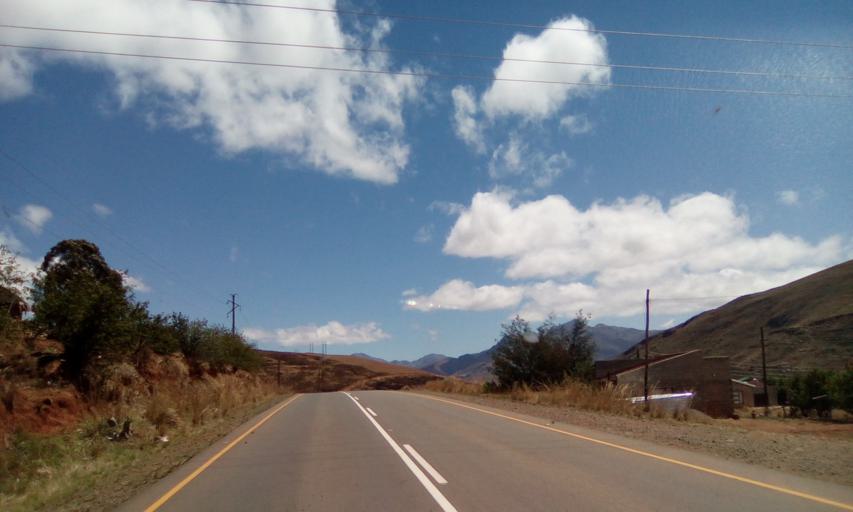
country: LS
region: Qacha's Nek
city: Qacha's Nek
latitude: -30.0913
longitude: 28.6429
